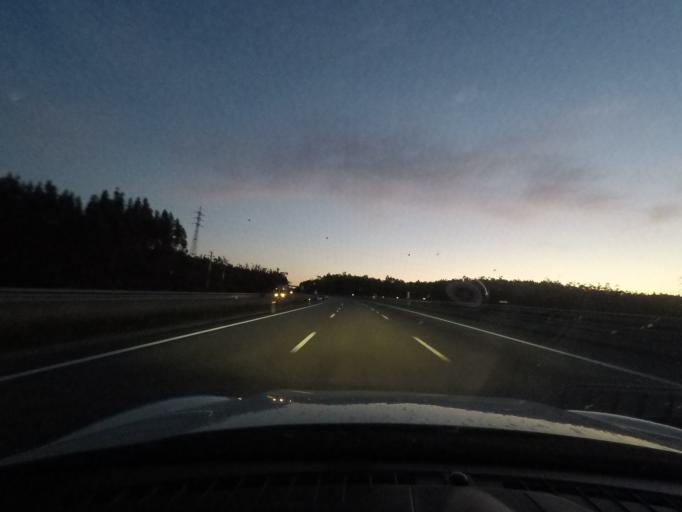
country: PT
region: Porto
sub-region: Vila Nova de Gaia
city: Sandim
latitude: 41.0586
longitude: -8.4665
